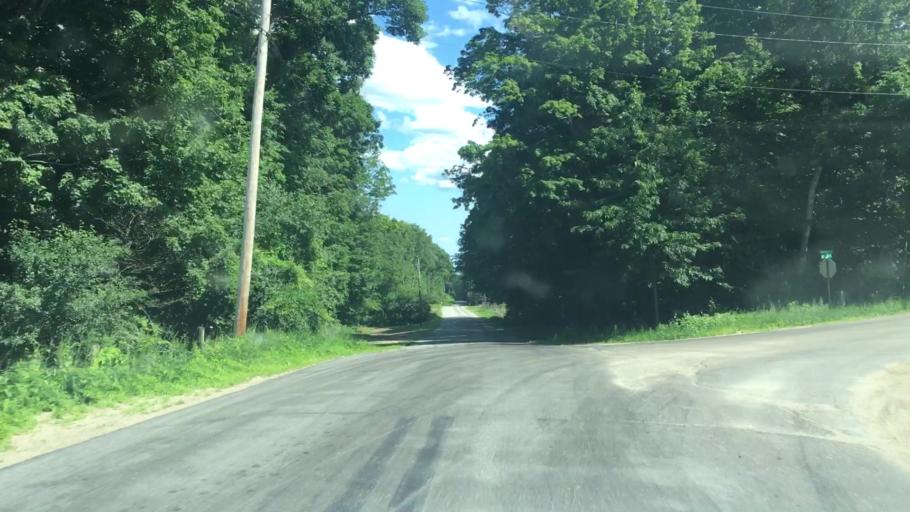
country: US
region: Maine
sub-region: Franklin County
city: Chesterville
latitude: 44.5675
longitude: -70.1459
